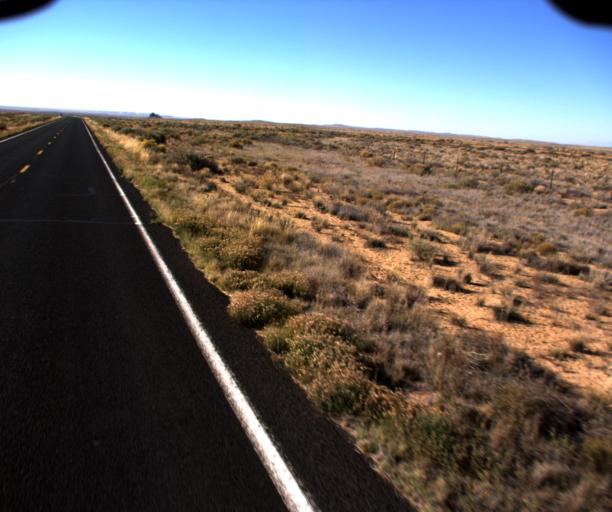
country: US
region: Arizona
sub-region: Navajo County
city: First Mesa
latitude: 35.7496
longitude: -110.5157
